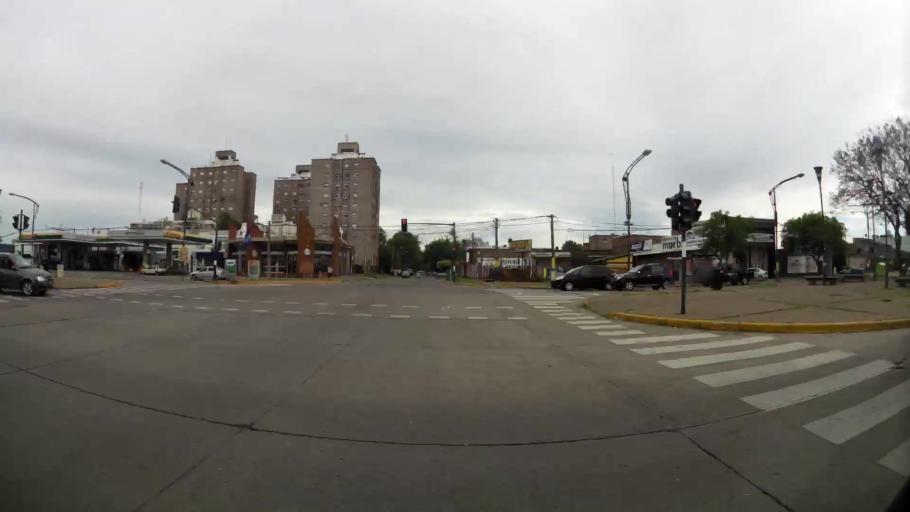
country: AR
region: Santa Fe
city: Gobernador Galvez
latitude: -32.9978
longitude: -60.6654
